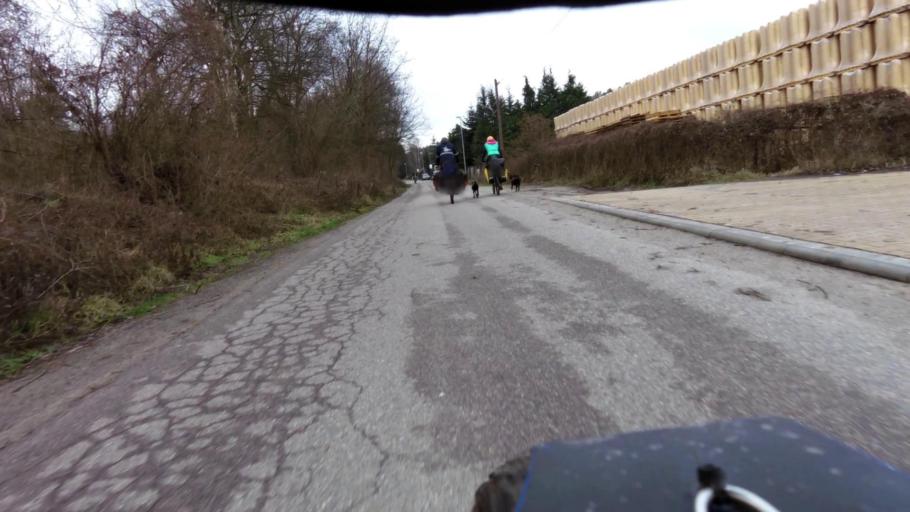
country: PL
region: Lubusz
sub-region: Powiat gorzowski
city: Jenin
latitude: 52.7096
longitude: 15.1317
